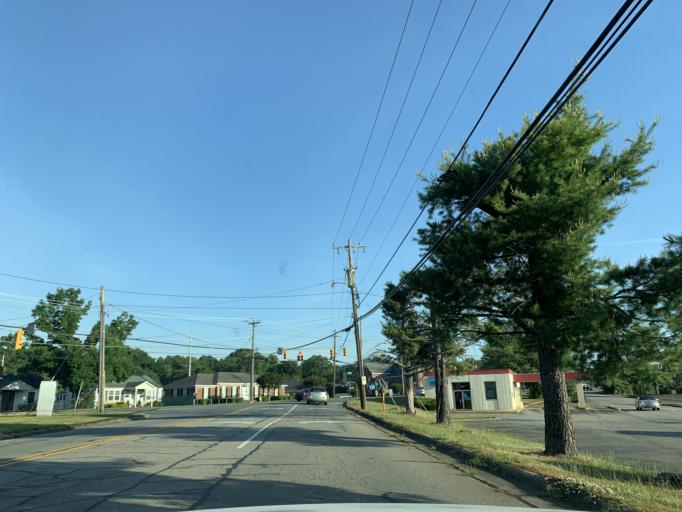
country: US
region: North Carolina
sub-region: Rockingham County
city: Reidsville
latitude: 36.3400
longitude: -79.6627
